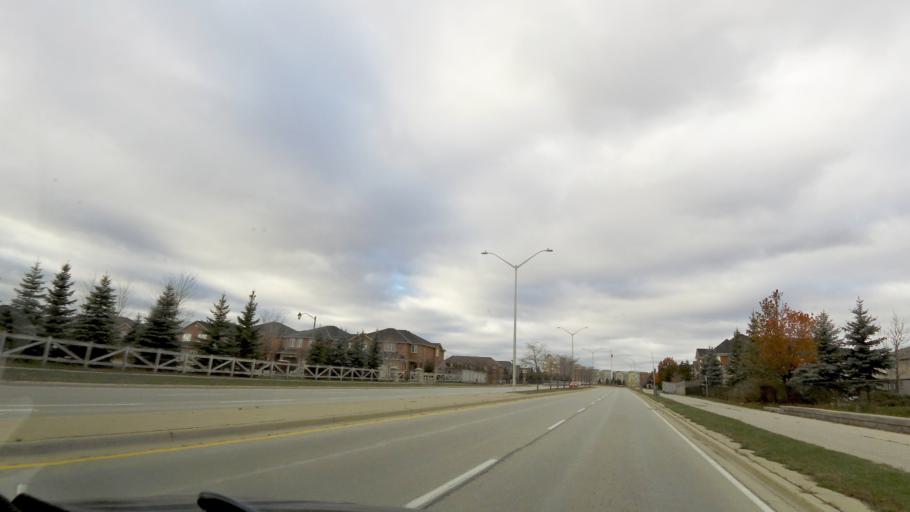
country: CA
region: Ontario
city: Oakville
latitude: 43.4441
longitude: -79.7523
